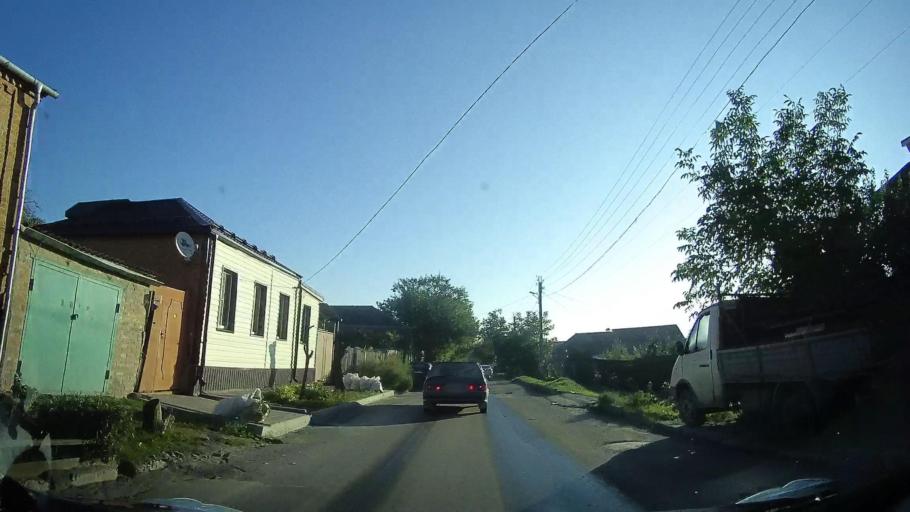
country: RU
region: Rostov
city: Severnyy
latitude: 47.2674
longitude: 39.6762
